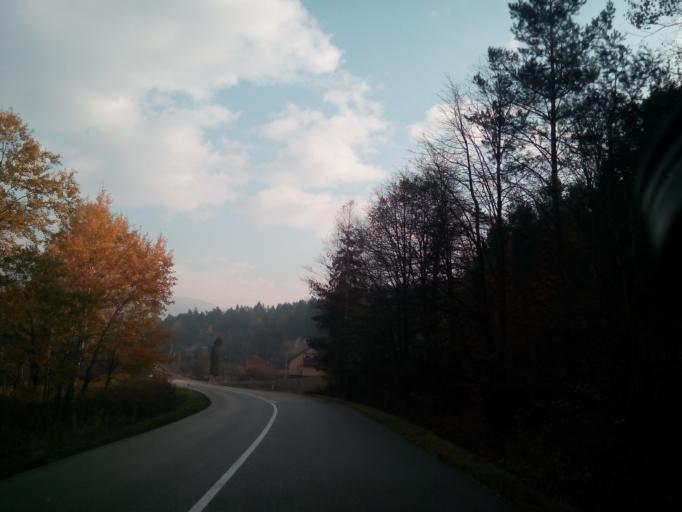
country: SK
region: Kosicky
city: Gelnica
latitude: 48.9116
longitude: 20.9409
